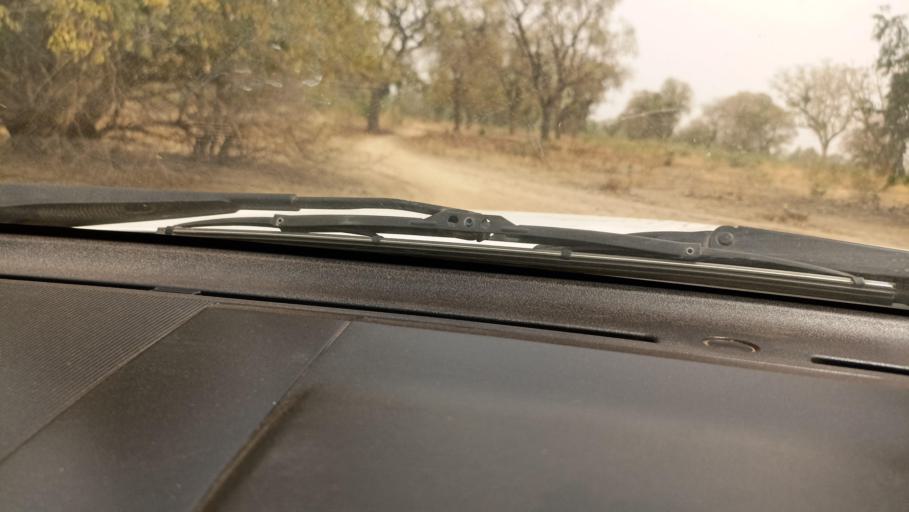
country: BF
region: Boucle du Mouhoun
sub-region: Province du Nayala
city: Toma
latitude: 12.8554
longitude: -2.8030
